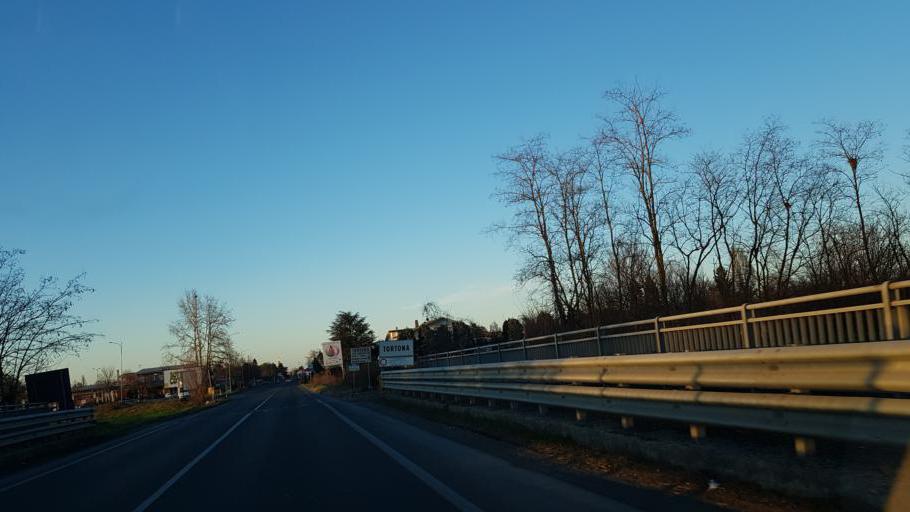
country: IT
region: Piedmont
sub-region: Provincia di Alessandria
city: Carbonara Scrivia
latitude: 44.8684
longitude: 8.8565
